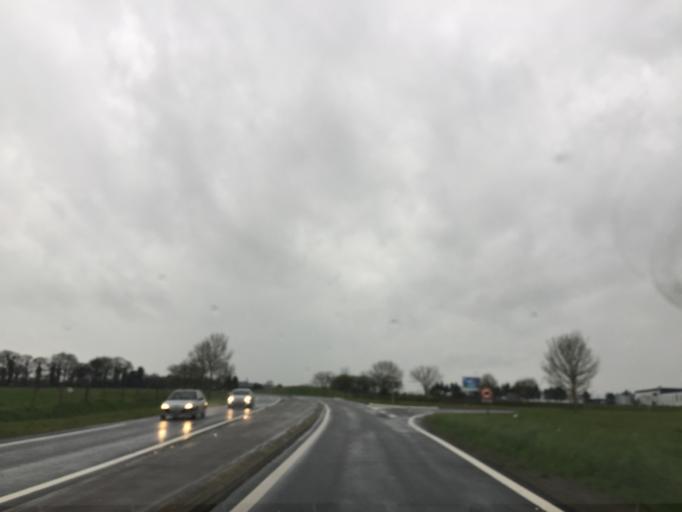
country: FR
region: Brittany
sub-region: Departement d'Ille-et-Vilaine
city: Javene
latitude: 48.3207
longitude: -1.1859
